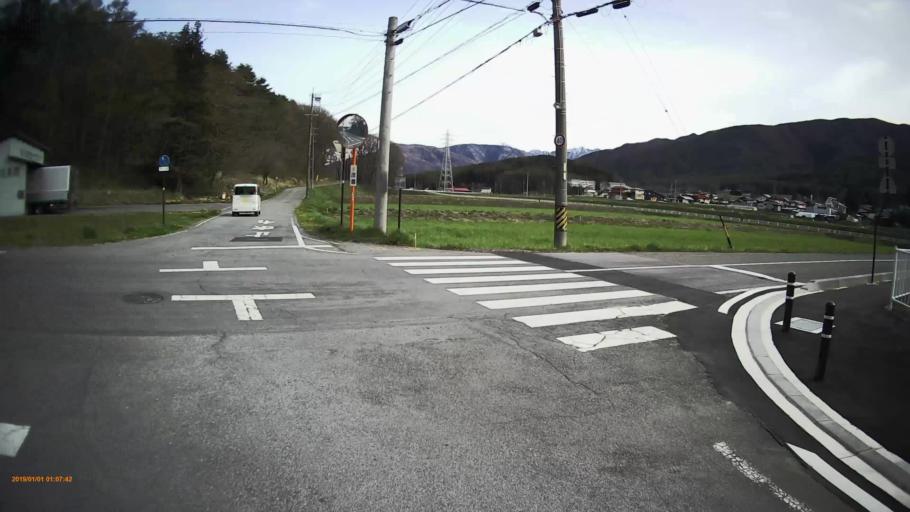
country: JP
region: Nagano
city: Chino
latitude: 35.9160
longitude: 138.2192
